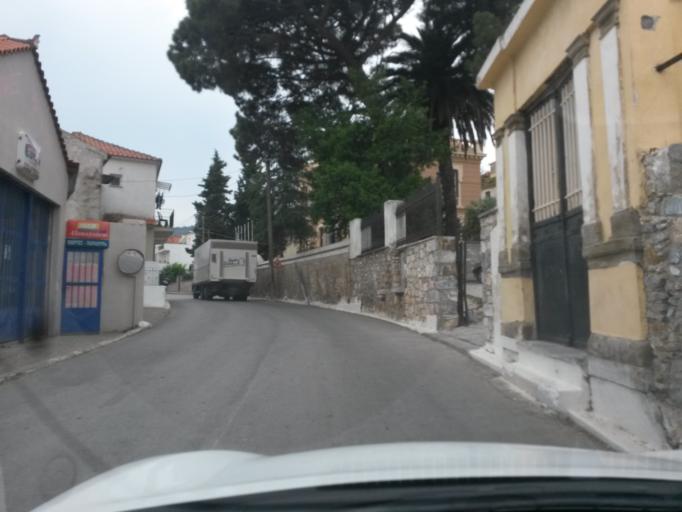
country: GR
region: North Aegean
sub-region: Nomos Lesvou
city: Pappados
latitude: 39.0403
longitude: 26.4554
